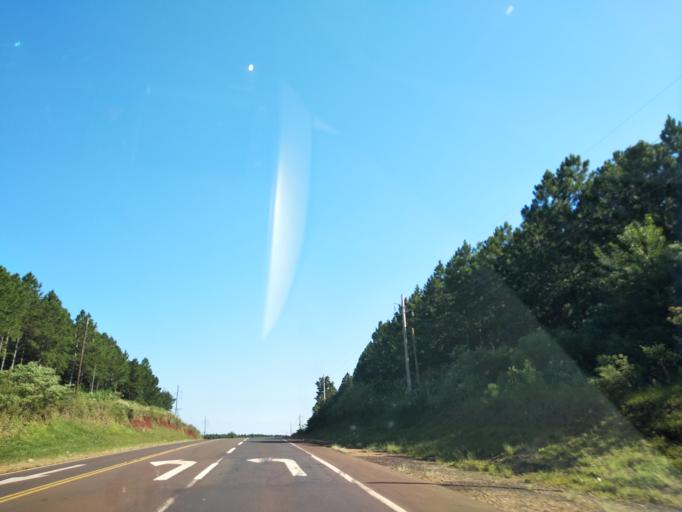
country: AR
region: Misiones
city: Capiovi
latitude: -26.8999
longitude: -55.0596
